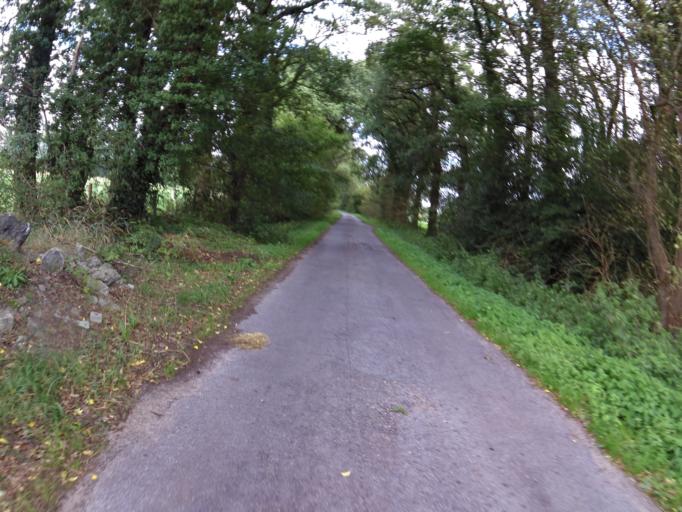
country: DE
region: North Rhine-Westphalia
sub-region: Regierungsbezirk Munster
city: Gronau
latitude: 52.1584
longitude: 7.0199
